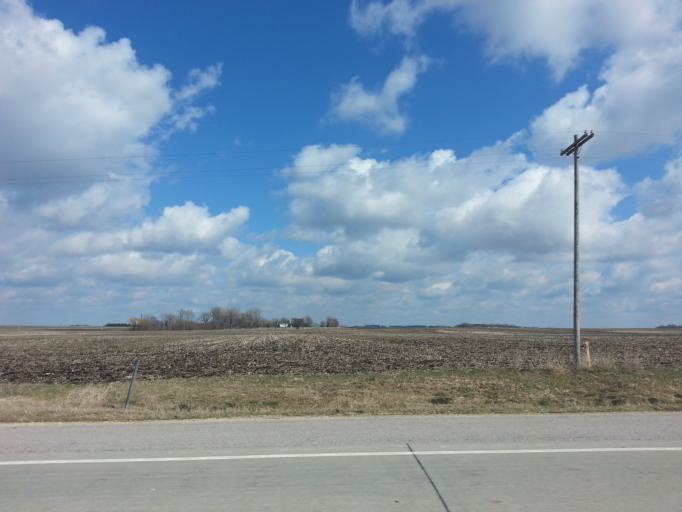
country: US
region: Minnesota
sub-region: Dodge County
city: Dodge Center
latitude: 44.1126
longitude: -92.8995
